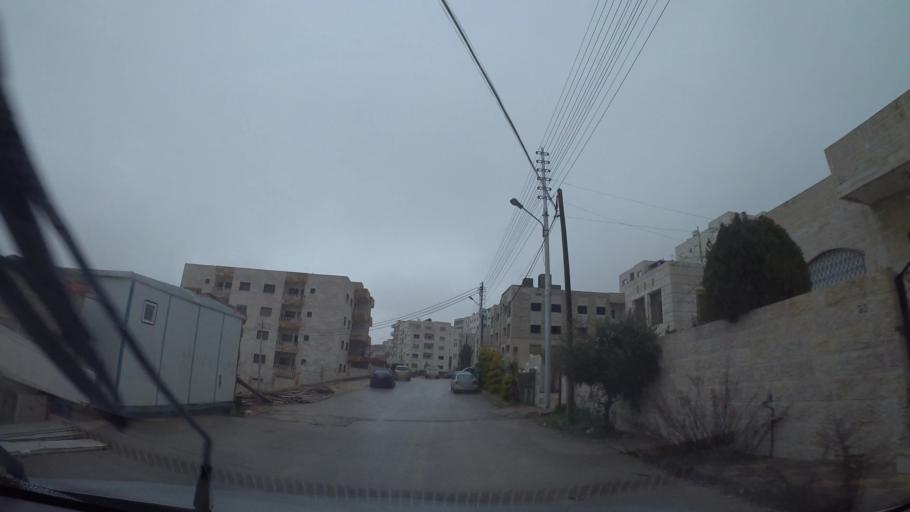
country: JO
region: Amman
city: Al Jubayhah
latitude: 32.0357
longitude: 35.8511
